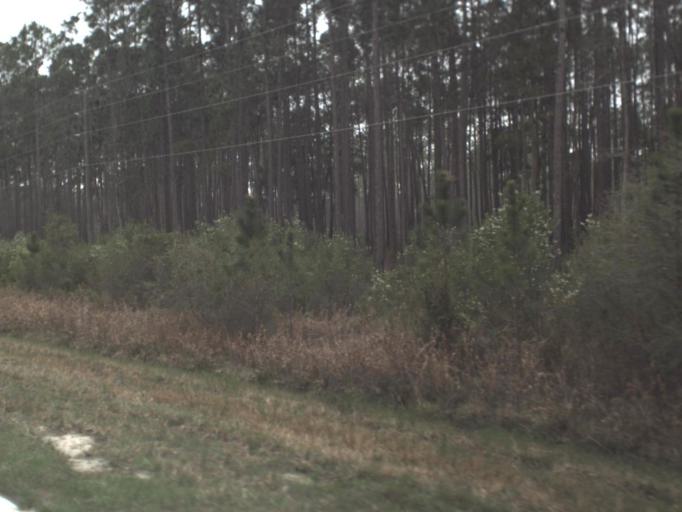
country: US
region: Florida
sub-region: Liberty County
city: Bristol
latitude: 30.2977
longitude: -84.8325
